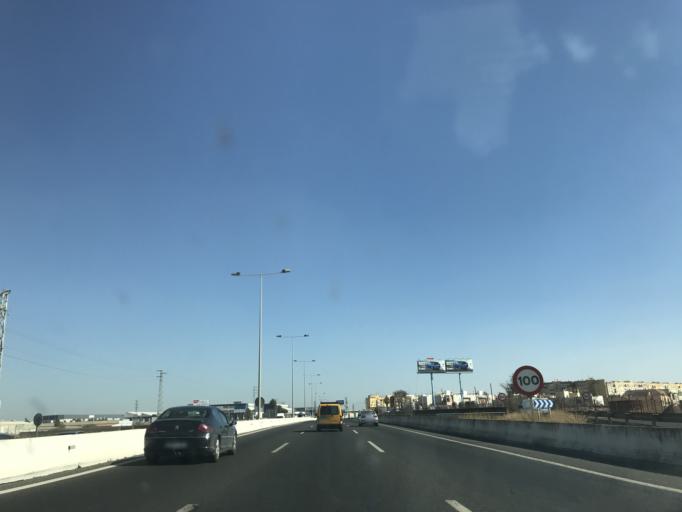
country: ES
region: Andalusia
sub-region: Provincia de Sevilla
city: Alcala de Guadaira
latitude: 37.3535
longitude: -5.8499
